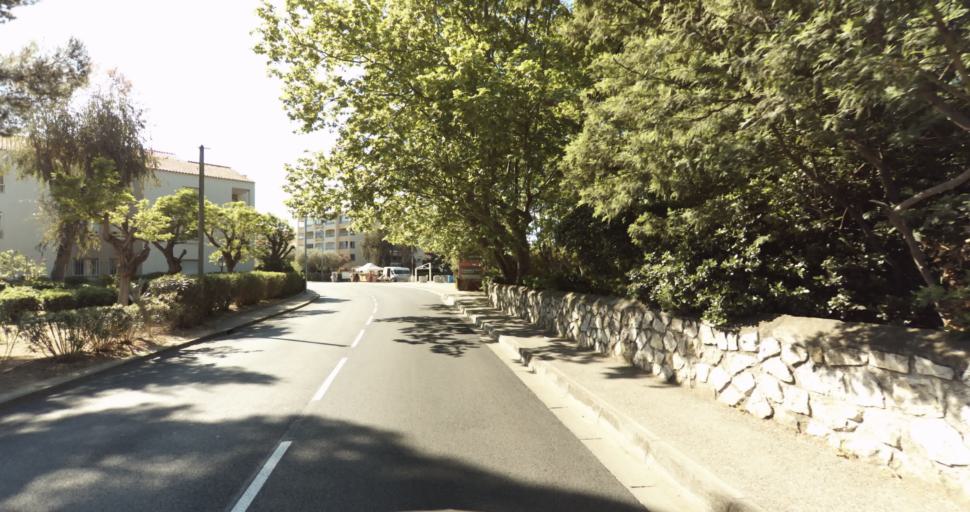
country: FR
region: Provence-Alpes-Cote d'Azur
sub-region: Departement du Var
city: Saint-Mandrier-sur-Mer
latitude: 43.0757
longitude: 5.9064
